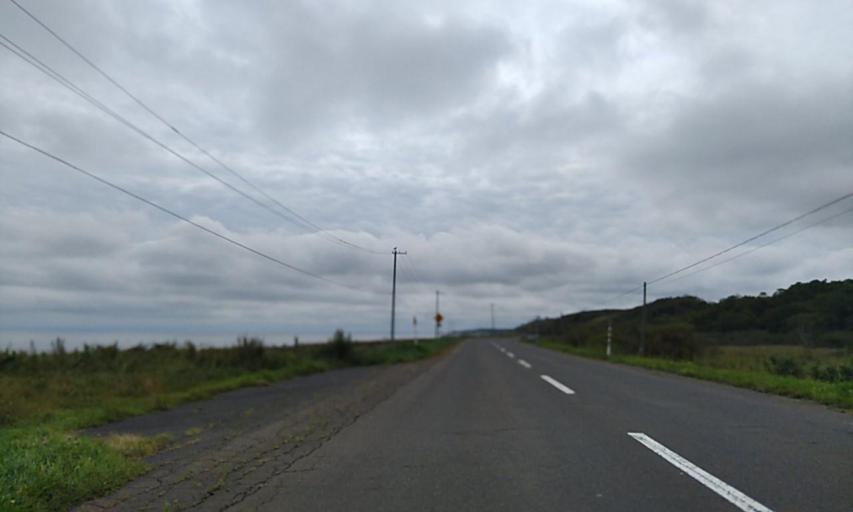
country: JP
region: Hokkaido
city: Shibetsu
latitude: 43.5100
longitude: 145.2451
